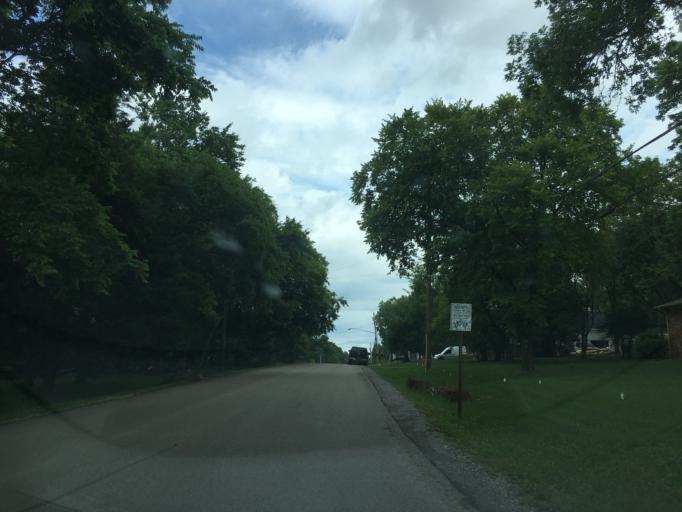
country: US
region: Tennessee
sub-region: Davidson County
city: Belle Meade
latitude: 36.0943
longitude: -86.8350
